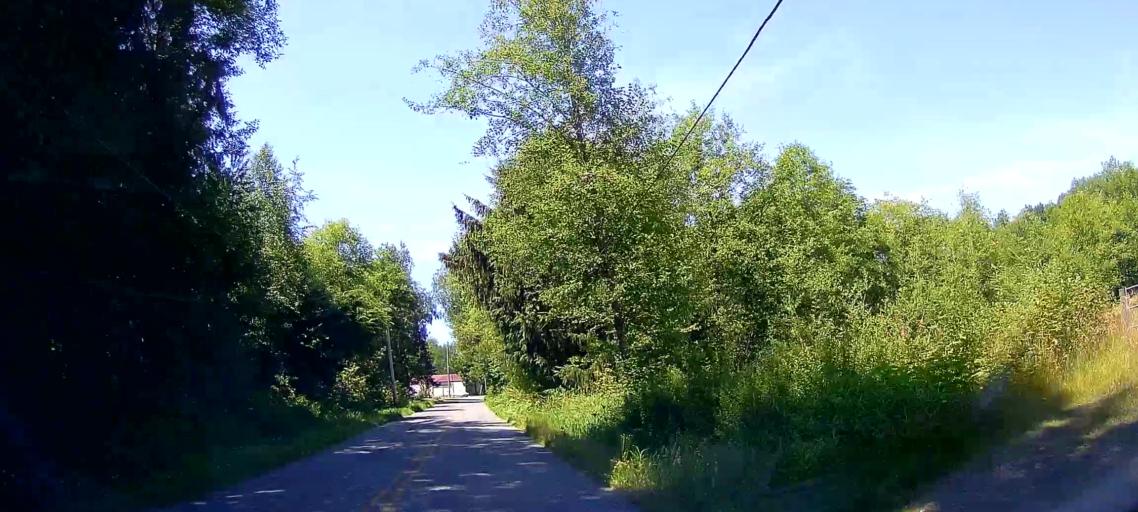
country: US
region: Washington
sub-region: Whatcom County
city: Sudden Valley
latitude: 48.6024
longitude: -122.3179
